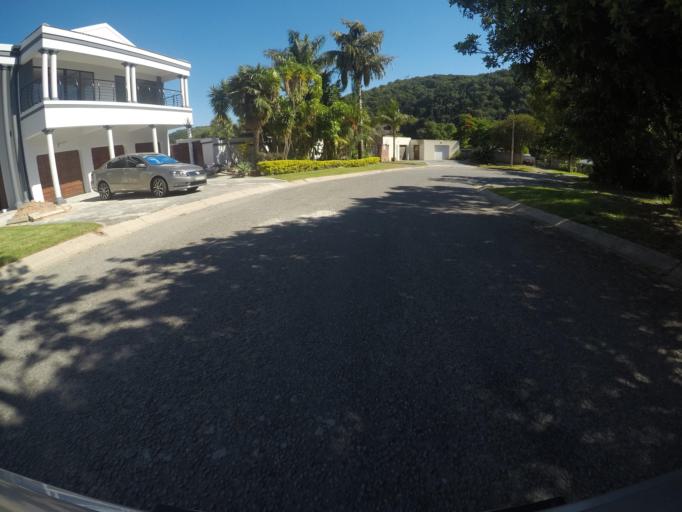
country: ZA
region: Eastern Cape
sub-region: Buffalo City Metropolitan Municipality
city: East London
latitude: -32.9428
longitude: 27.8975
